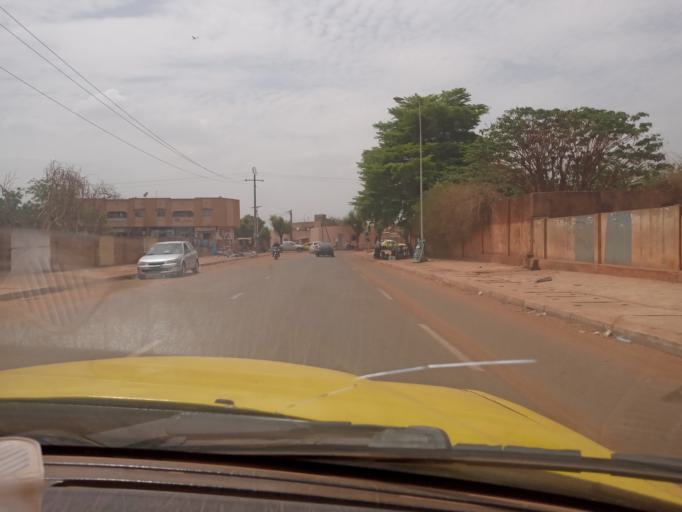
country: ML
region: Bamako
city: Bamako
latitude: 12.6032
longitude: -7.9624
